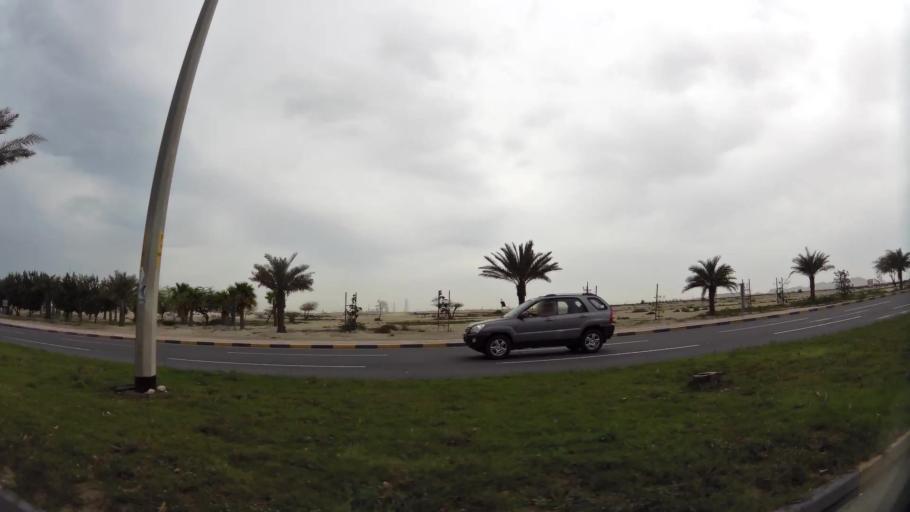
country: BH
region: Central Governorate
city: Dar Kulayb
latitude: 26.0782
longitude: 50.5392
